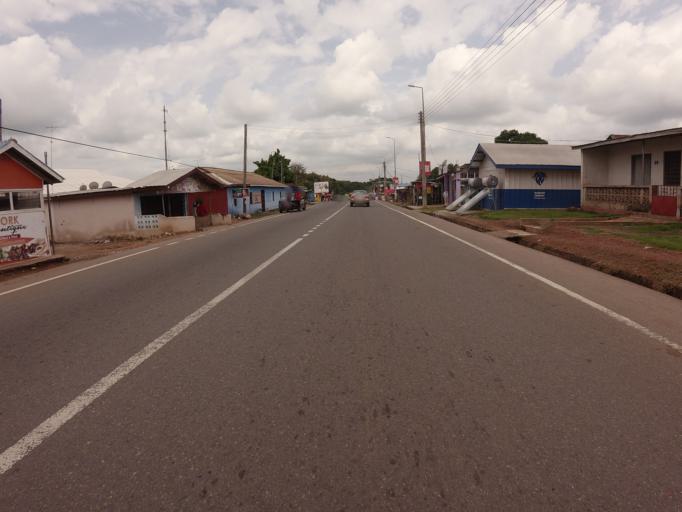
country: GH
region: Volta
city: Ho
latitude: 6.6017
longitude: 0.4711
